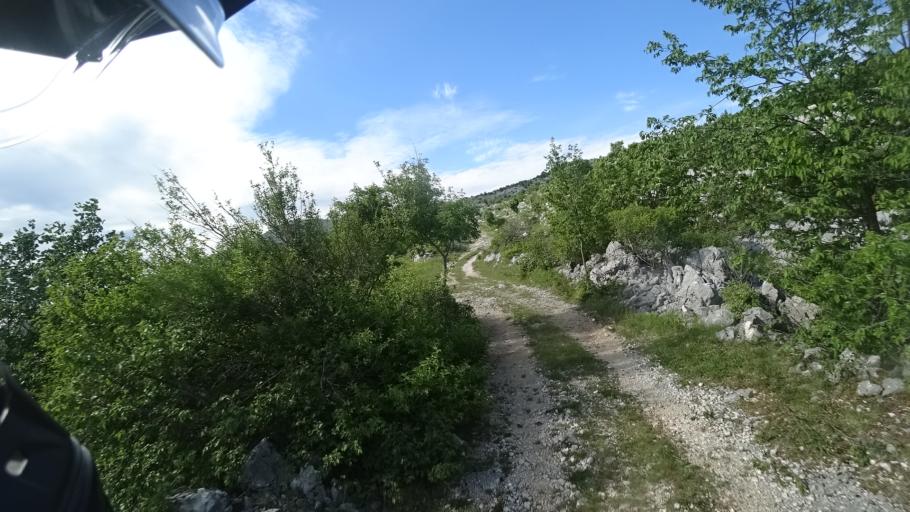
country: HR
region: Splitsko-Dalmatinska
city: Hrvace
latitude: 43.7941
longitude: 16.4341
